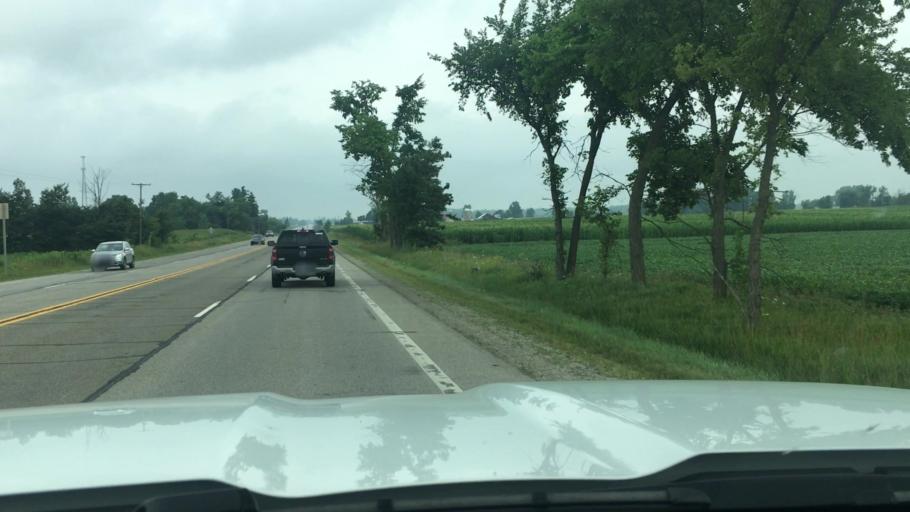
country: US
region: Michigan
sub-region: Sanilac County
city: Brown City
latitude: 43.2167
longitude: -83.0775
